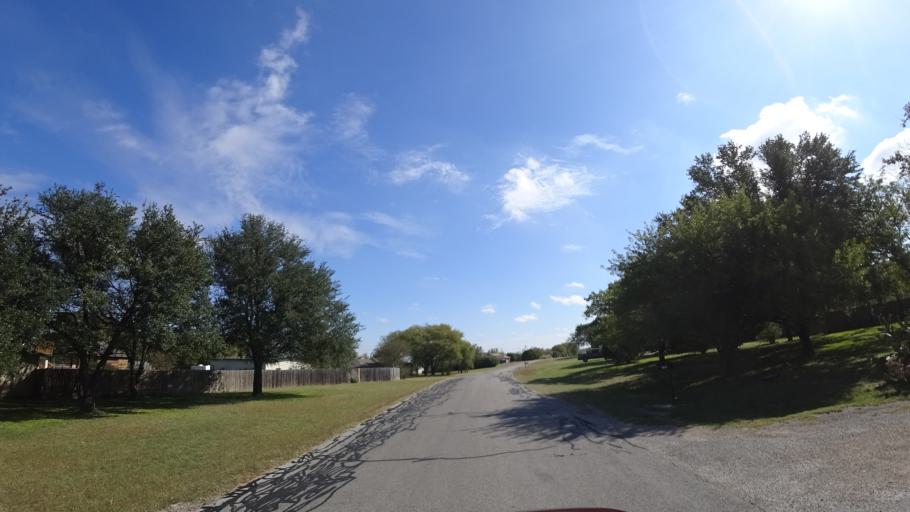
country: US
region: Texas
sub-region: Travis County
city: Windemere
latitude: 30.4519
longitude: -97.6515
